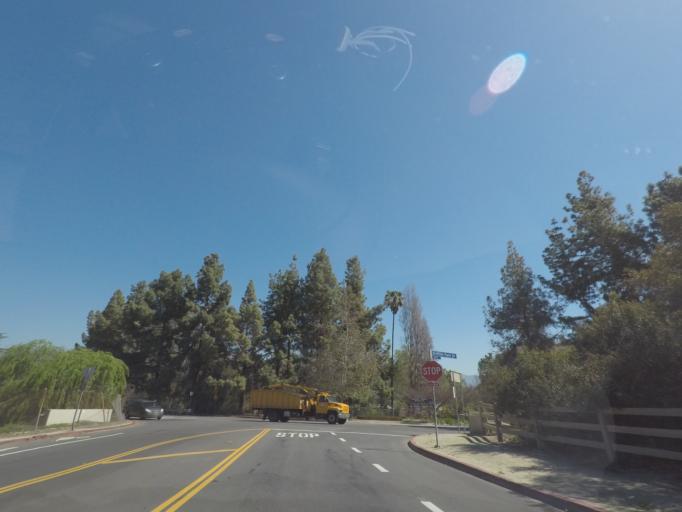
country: US
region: California
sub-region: Los Angeles County
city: Burbank
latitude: 34.1535
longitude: -118.3095
